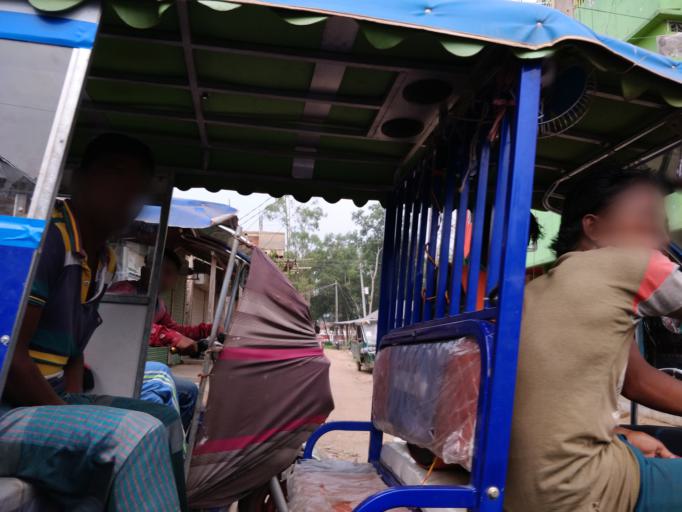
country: BD
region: Sylhet
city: Habiganj
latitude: 24.1683
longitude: 91.3546
